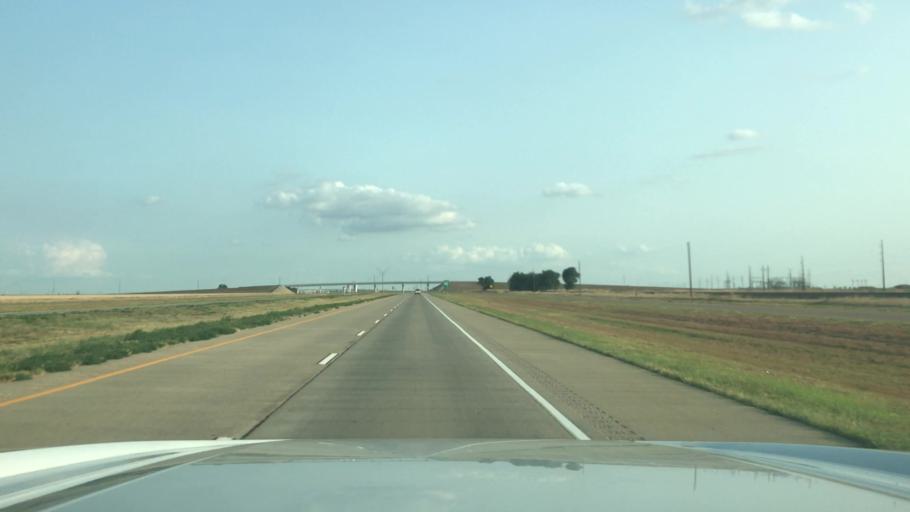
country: US
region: Texas
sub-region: Swisher County
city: Tulia
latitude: 34.6545
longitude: -101.8291
